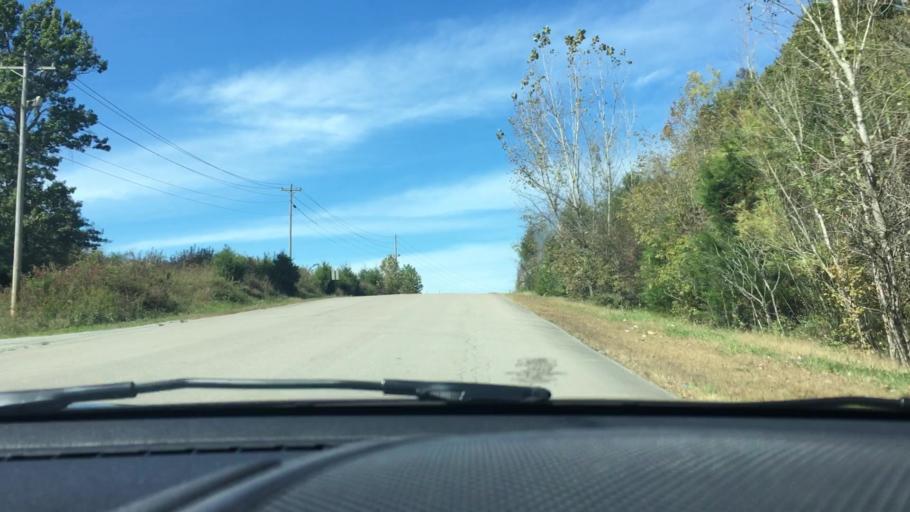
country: US
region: Tennessee
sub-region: Giles County
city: Pulaski
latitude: 35.2228
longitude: -87.0665
